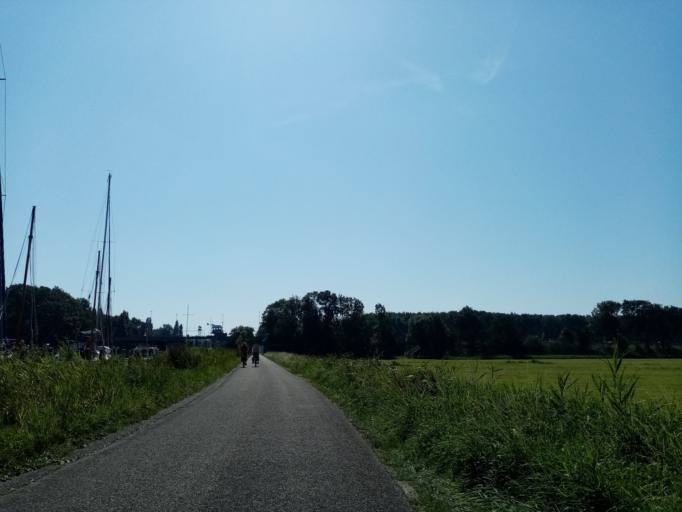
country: NL
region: South Holland
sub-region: Gemeente Teylingen
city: Sassenheim
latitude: 52.2257
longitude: 4.5507
